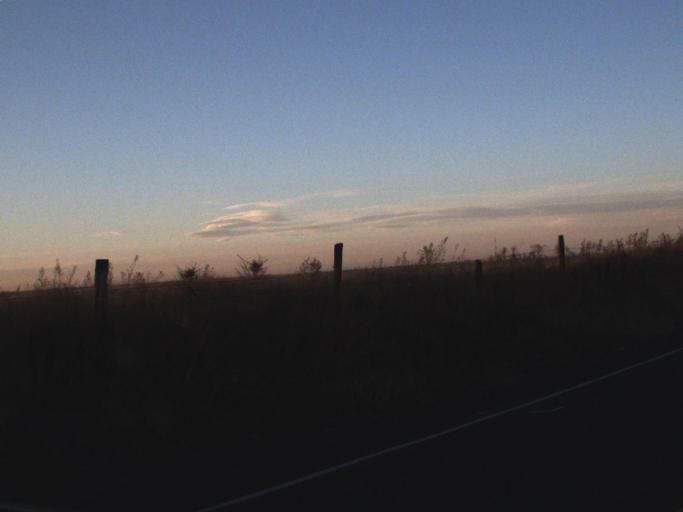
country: US
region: Washington
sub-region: Adams County
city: Ritzville
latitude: 47.0687
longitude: -118.6630
